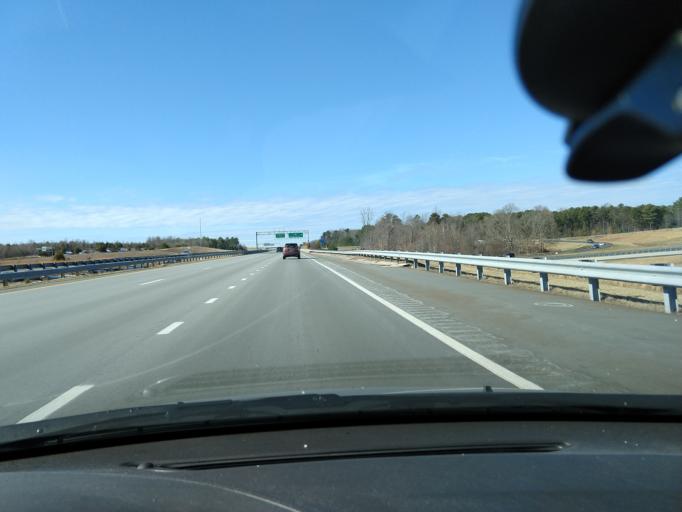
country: US
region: North Carolina
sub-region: Guilford County
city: Summerfield
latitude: 36.1166
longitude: -79.9063
